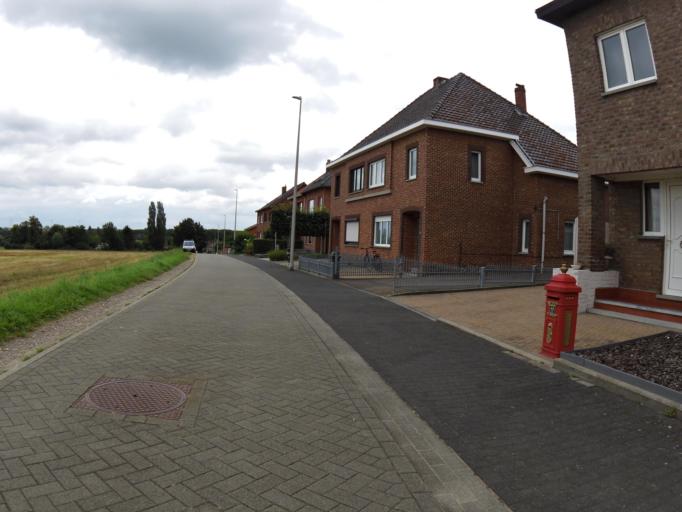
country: BE
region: Flanders
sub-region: Provincie Limburg
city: Tongeren
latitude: 50.7865
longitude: 5.4997
